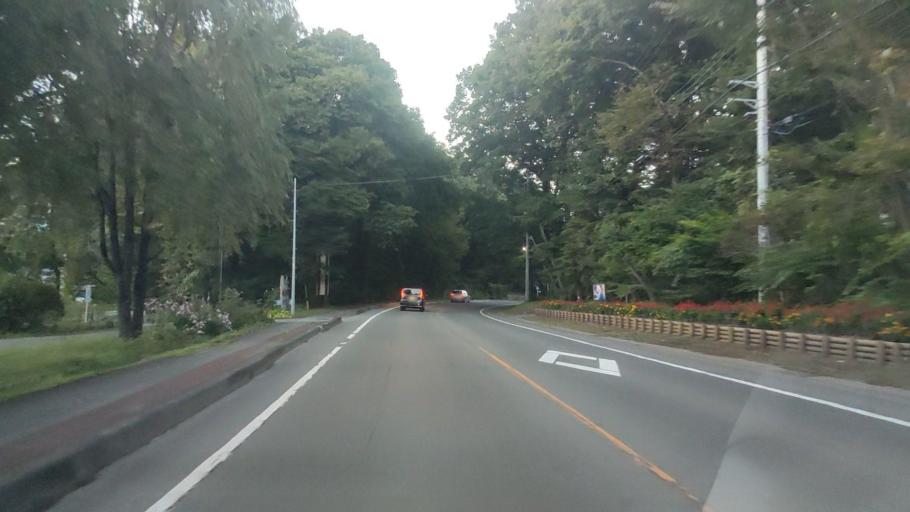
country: JP
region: Nagano
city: Komoro
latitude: 36.5020
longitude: 138.5899
